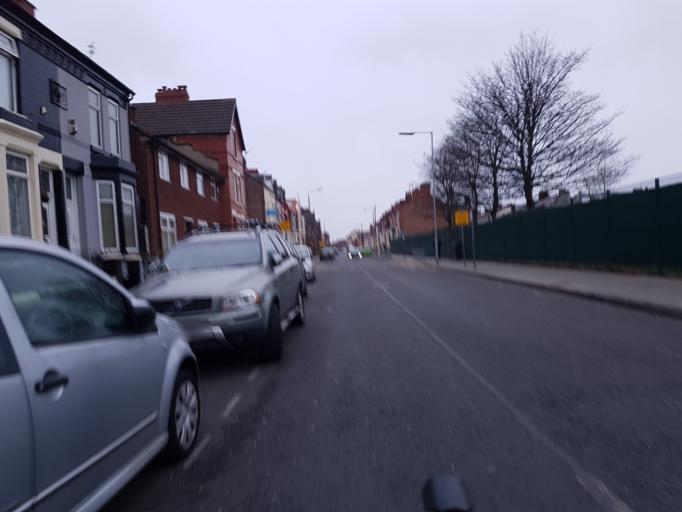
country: GB
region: England
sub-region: Liverpool
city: Liverpool
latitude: 53.4433
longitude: -2.9715
